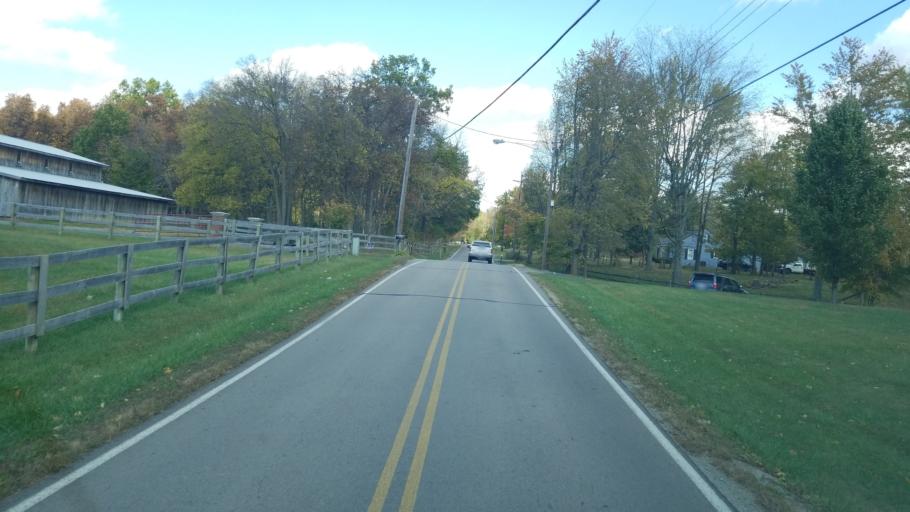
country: US
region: Ohio
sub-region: Warren County
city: Morrow
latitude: 39.3887
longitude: -84.1594
